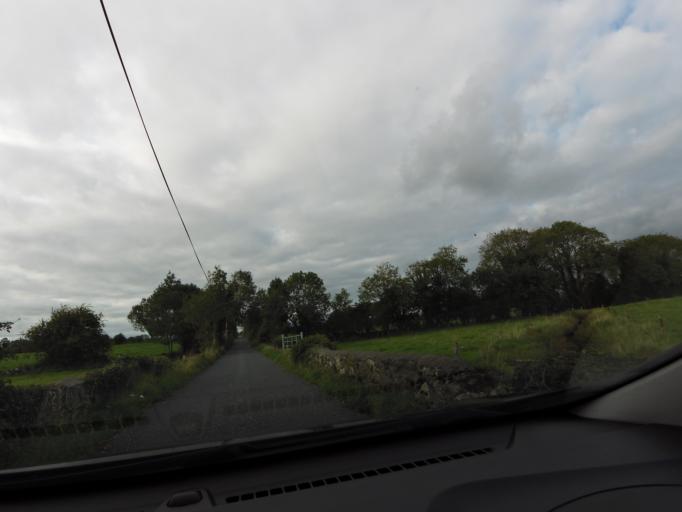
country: IE
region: Connaught
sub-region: County Galway
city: Ballinasloe
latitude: 53.3470
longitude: -8.0933
